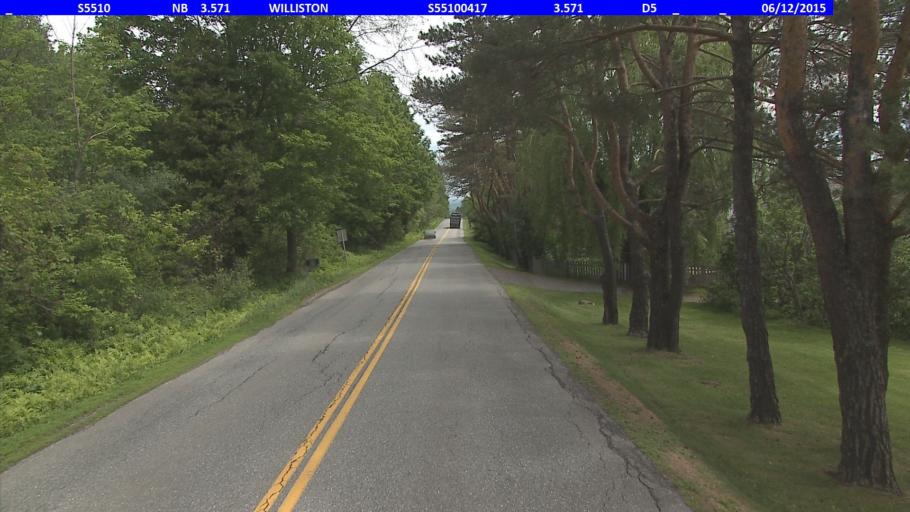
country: US
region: Vermont
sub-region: Chittenden County
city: Williston
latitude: 44.4213
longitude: -73.0806
